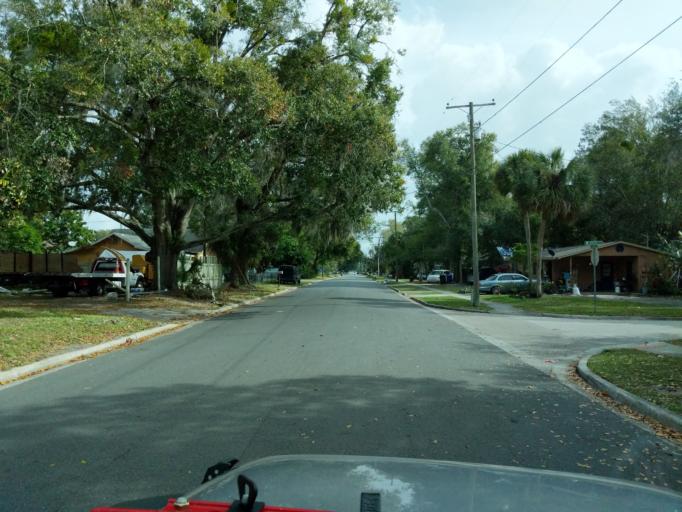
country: US
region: Florida
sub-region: Orange County
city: Winter Garden
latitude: 28.5619
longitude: -81.5820
